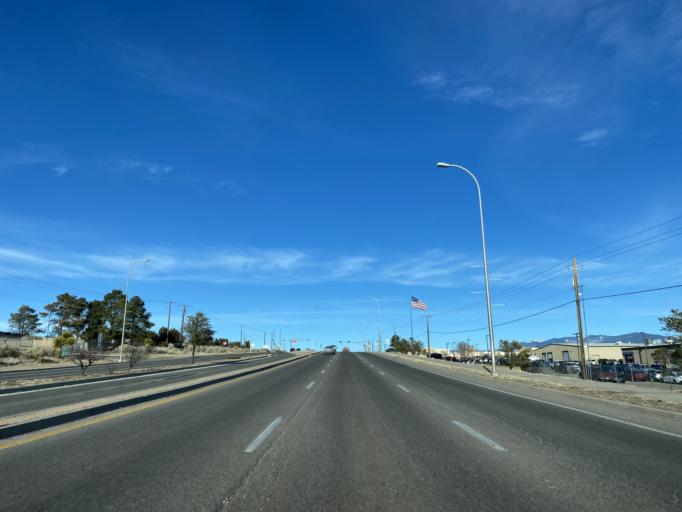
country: US
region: New Mexico
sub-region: Santa Fe County
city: Agua Fria
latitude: 35.6280
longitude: -106.0240
